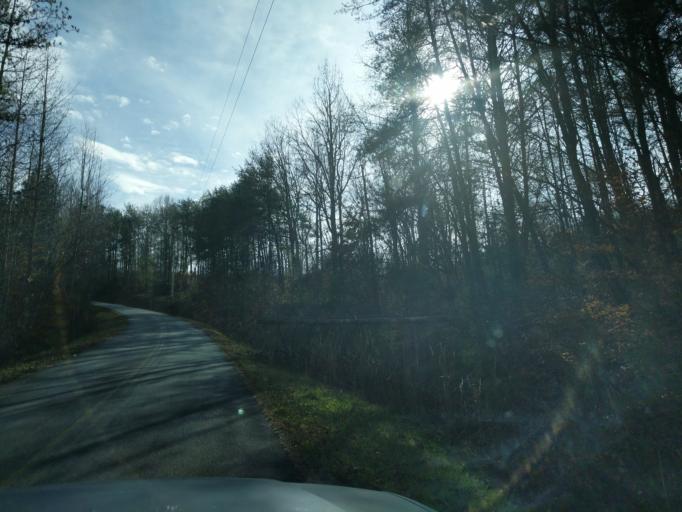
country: US
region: South Carolina
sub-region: Oconee County
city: Walhalla
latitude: 34.8514
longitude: -83.0532
